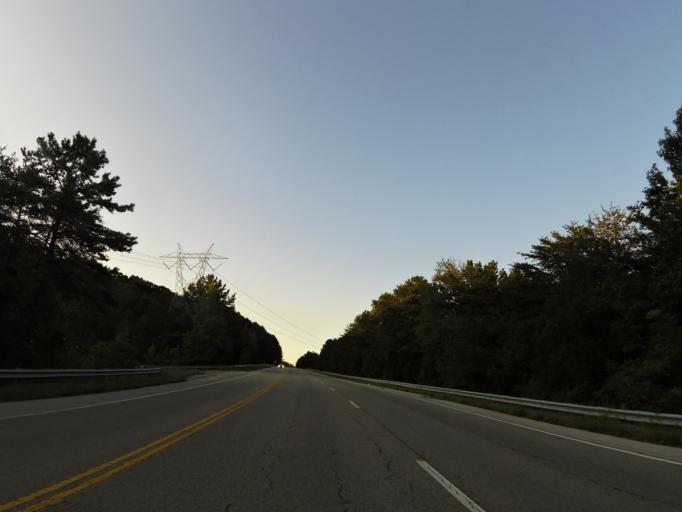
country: US
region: Tennessee
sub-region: Roane County
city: Midtown
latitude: 35.8247
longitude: -84.5469
